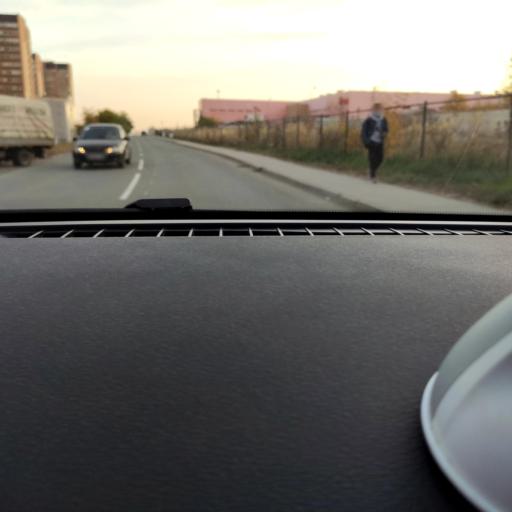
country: RU
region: Samara
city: Samara
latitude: 53.2098
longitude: 50.2029
